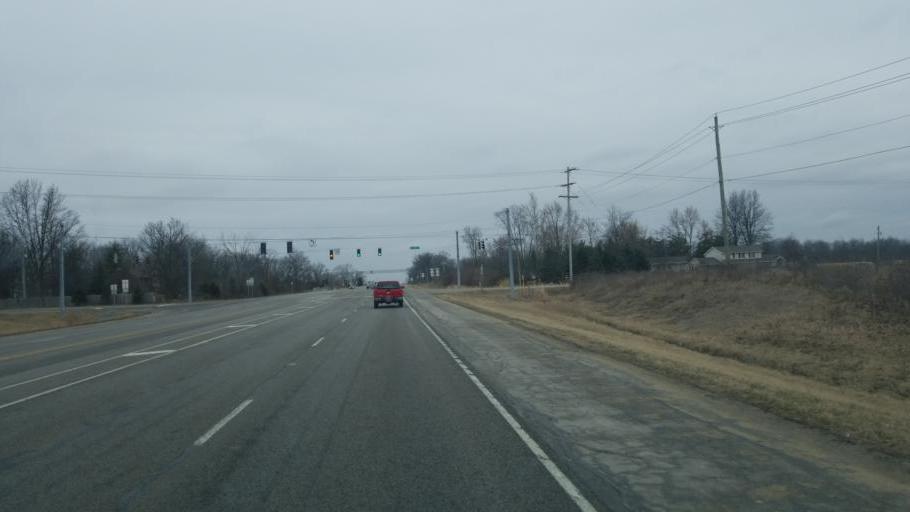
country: US
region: Indiana
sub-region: Adams County
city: Decatur
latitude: 40.8042
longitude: -84.9374
